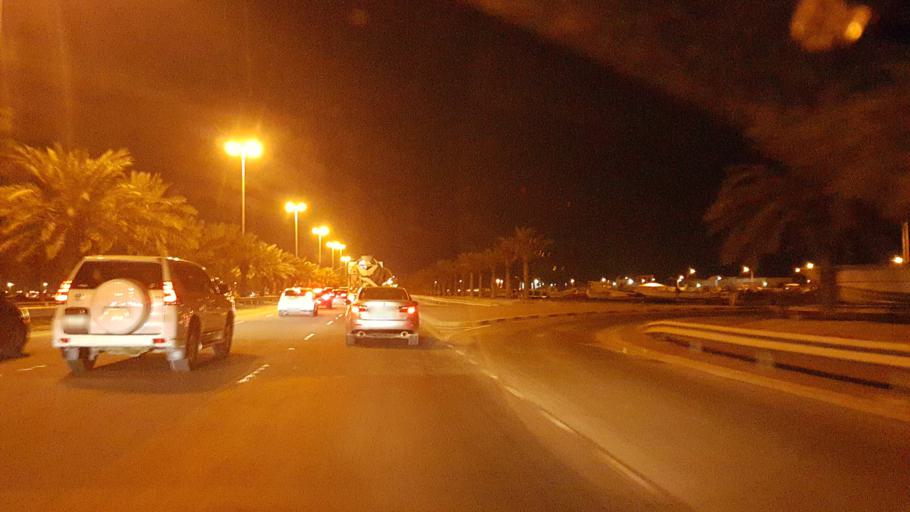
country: BH
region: Muharraq
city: Al Hadd
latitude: 26.2476
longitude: 50.6589
